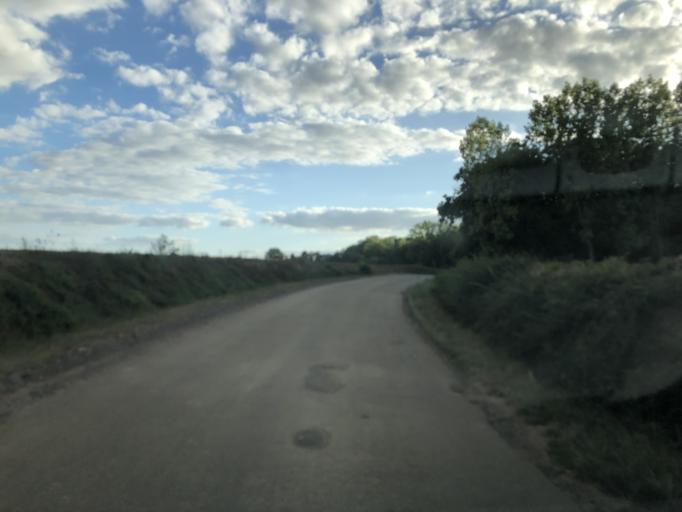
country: FR
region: Bourgogne
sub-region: Departement de l'Yonne
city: Fleury-la-Vallee
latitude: 47.8576
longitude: 3.4365
